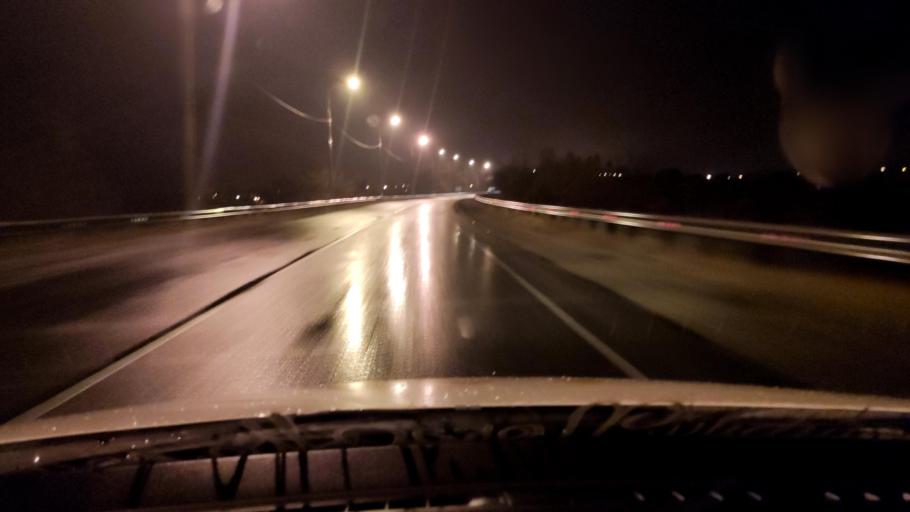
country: RU
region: Voronezj
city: Pridonskoy
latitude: 51.7164
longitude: 39.0744
